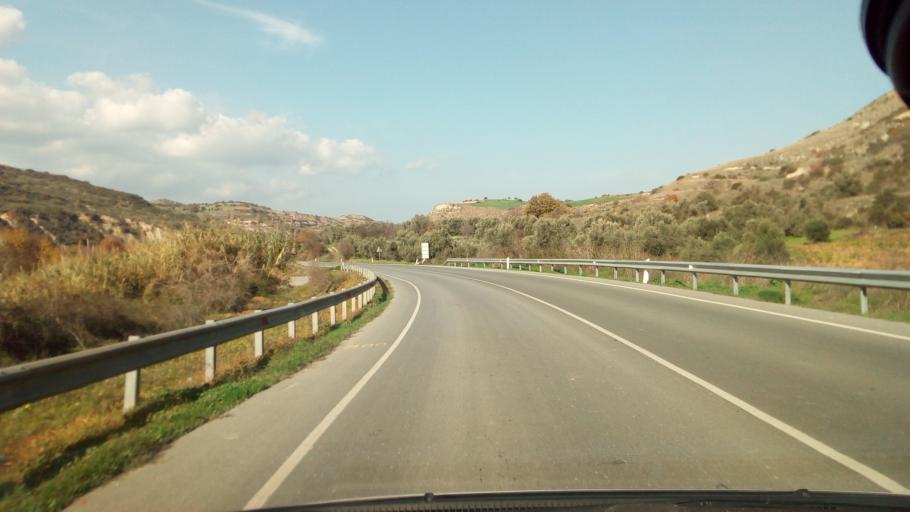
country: CY
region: Pafos
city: Polis
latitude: 34.9549
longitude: 32.4671
